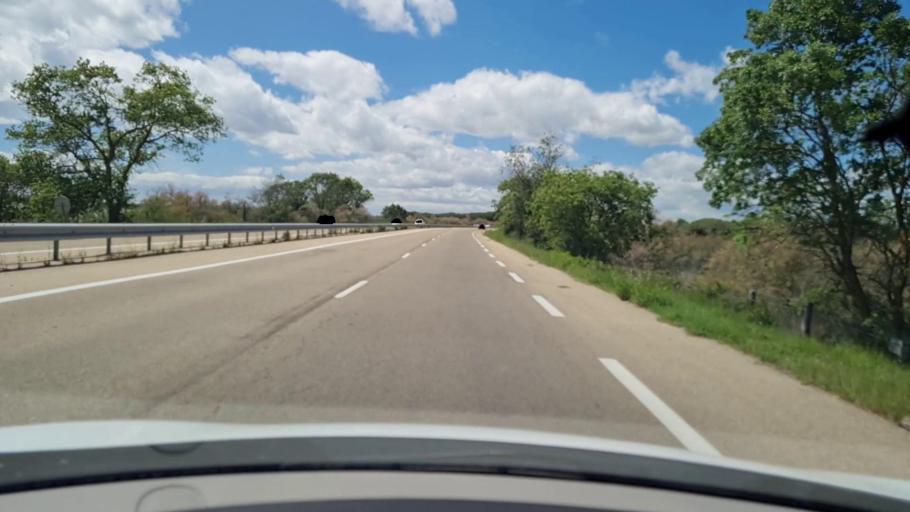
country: FR
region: Languedoc-Roussillon
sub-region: Departement du Gard
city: Le Grau-du-Roi
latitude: 43.5625
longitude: 4.1373
